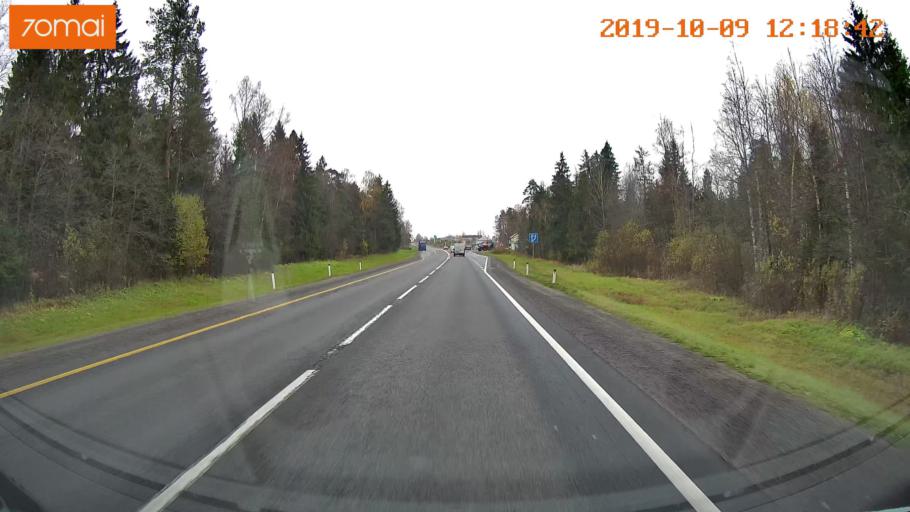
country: RU
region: Jaroslavl
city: Prechistoye
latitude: 58.4386
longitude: 40.3214
